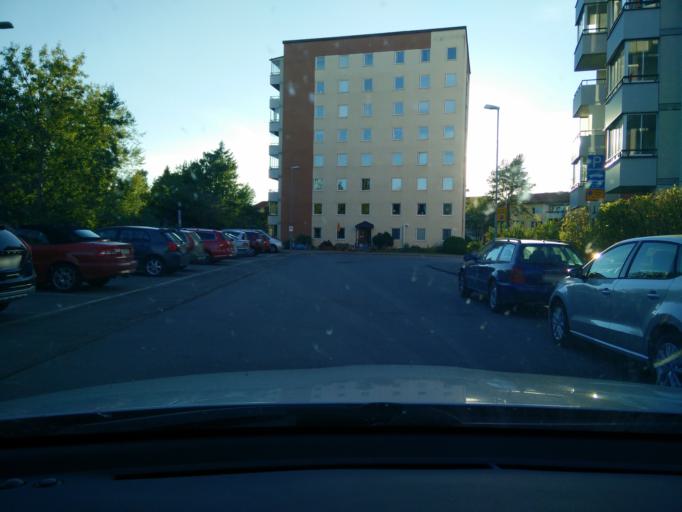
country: SE
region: Stockholm
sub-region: Sollentuna Kommun
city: Sollentuna
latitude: 59.4473
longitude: 17.9625
